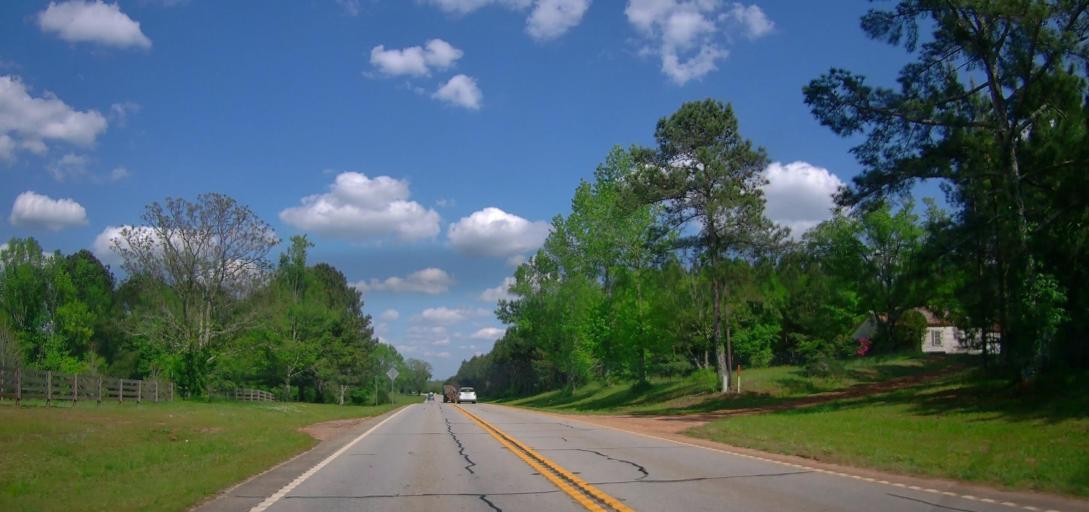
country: US
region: Georgia
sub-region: Greene County
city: Greensboro
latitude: 33.5710
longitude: -83.2327
